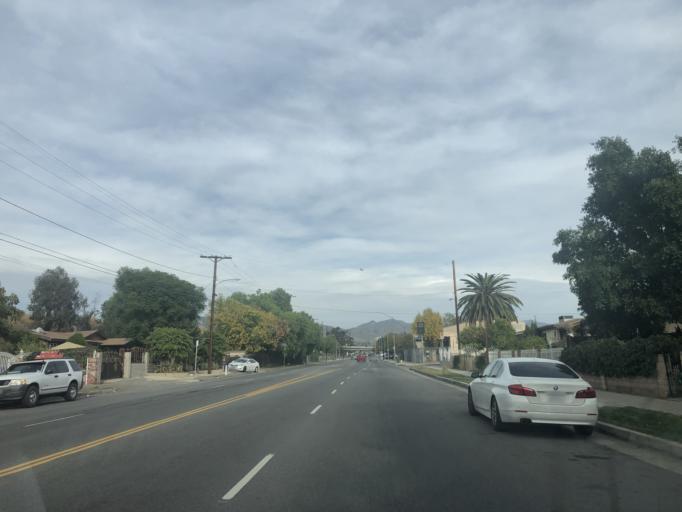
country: US
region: California
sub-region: Los Angeles County
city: San Fernando
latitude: 34.2679
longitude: -118.4342
